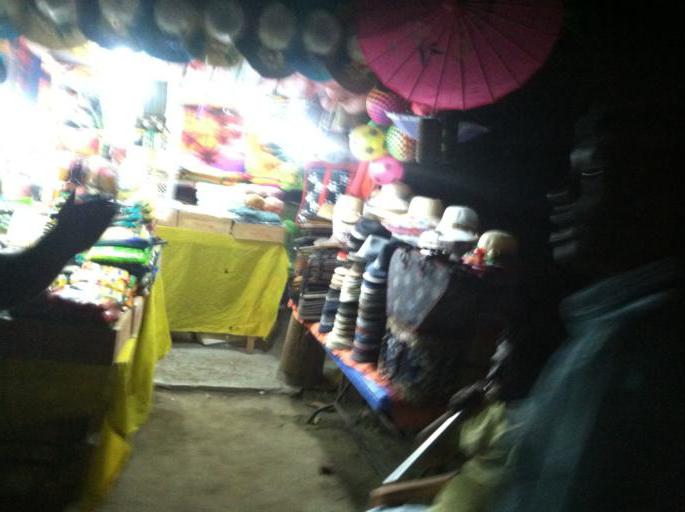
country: BD
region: Chittagong
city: Teknaf
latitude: 20.9201
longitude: 92.2681
